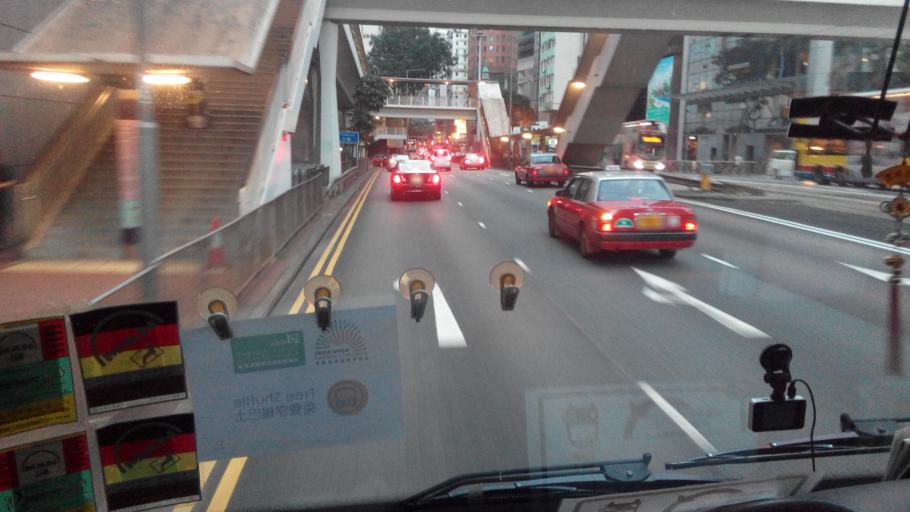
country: HK
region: Wanchai
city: Wan Chai
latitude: 22.2754
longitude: 114.1653
